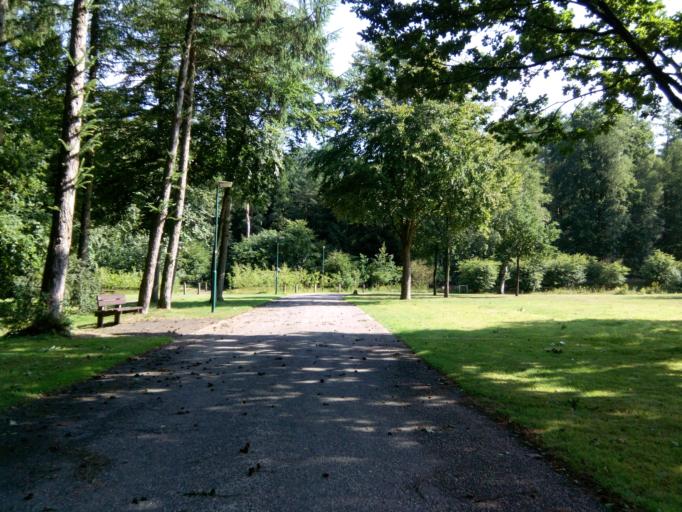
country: NL
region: Utrecht
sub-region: Gemeente Utrechtse Heuvelrug
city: Doorn
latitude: 52.0472
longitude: 5.3308
